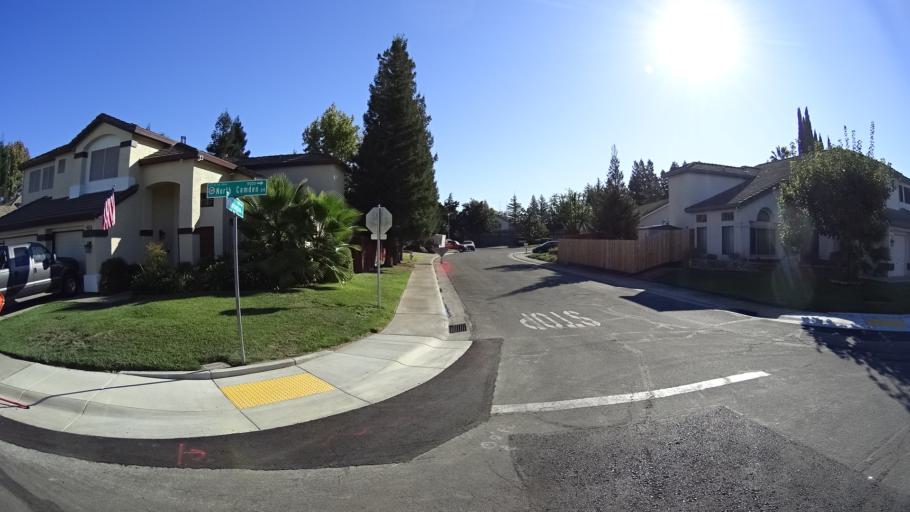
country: US
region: California
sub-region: Sacramento County
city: Elk Grove
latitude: 38.4306
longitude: -121.3746
